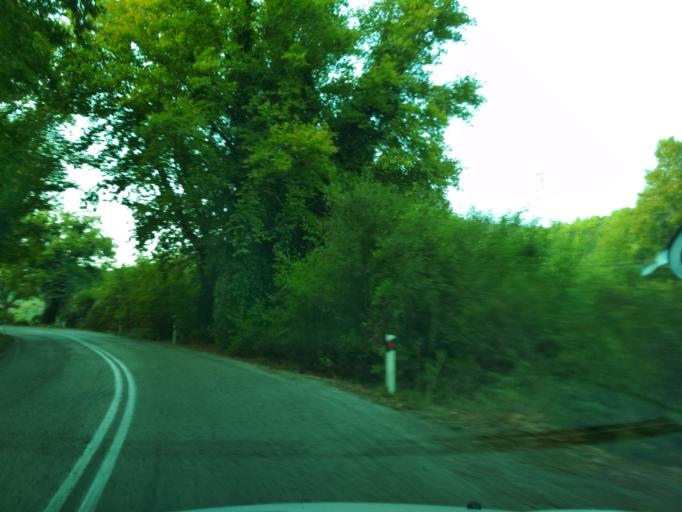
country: GR
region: Central Greece
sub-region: Nomos Evvoias
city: Prokopion
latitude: 38.7615
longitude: 23.4789
